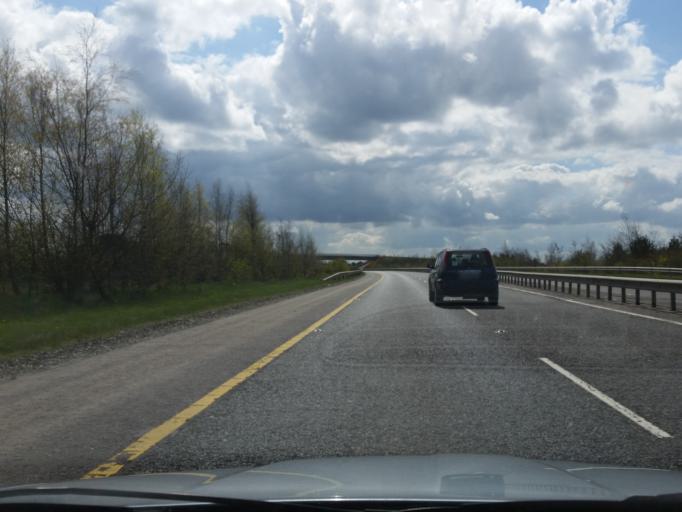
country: IE
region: Leinster
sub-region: An Mhi
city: Ashbourne
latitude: 53.5142
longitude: -6.4205
